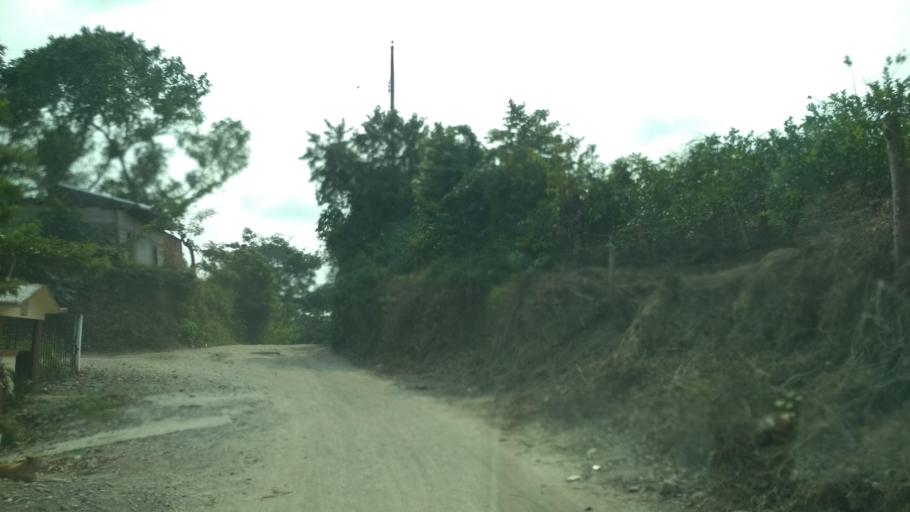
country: MM
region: Kayah
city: Loikaw
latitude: 20.2140
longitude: 97.2848
